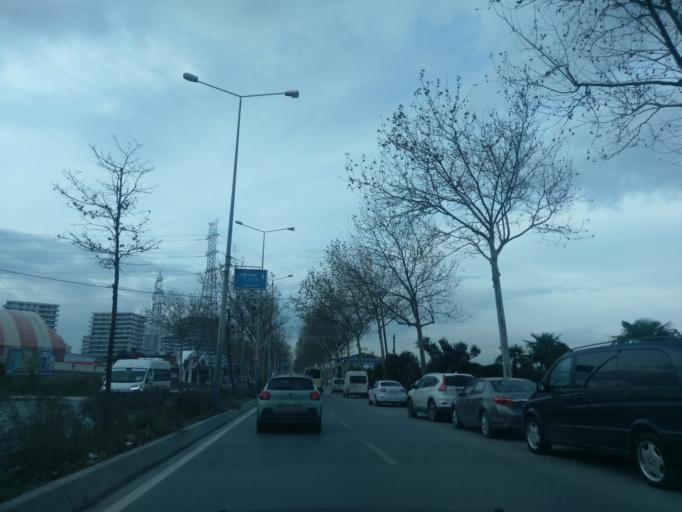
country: TR
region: Istanbul
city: Esenyurt
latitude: 41.0666
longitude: 28.6699
